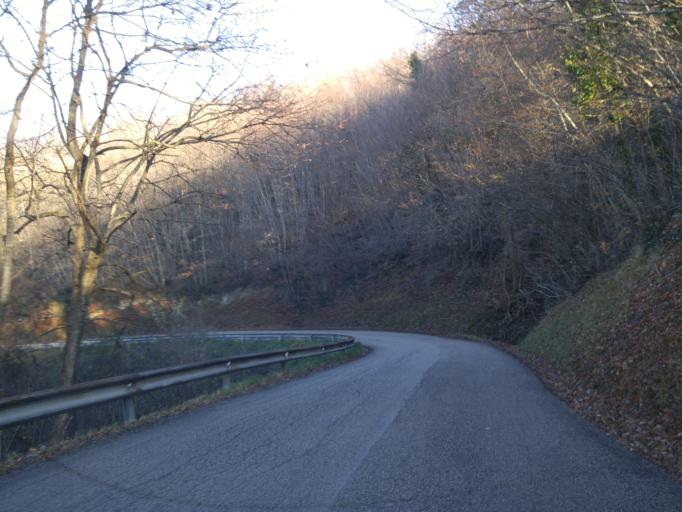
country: IT
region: The Marches
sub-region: Provincia di Pesaro e Urbino
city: Isola del Piano
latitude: 43.7263
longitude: 12.7477
